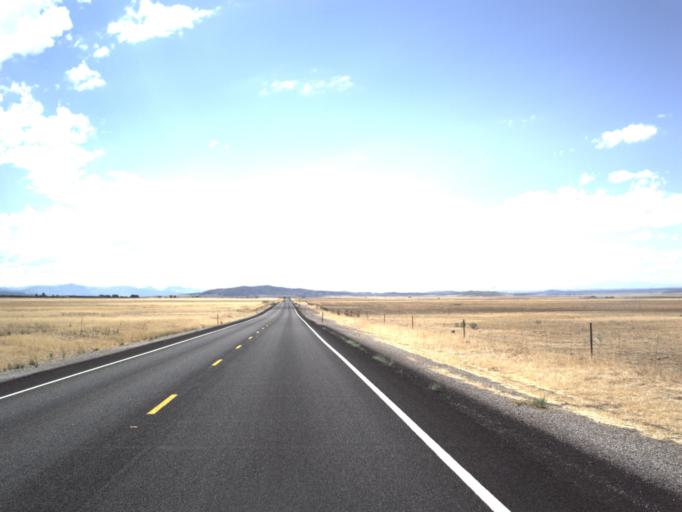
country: US
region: Utah
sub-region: Millard County
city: Fillmore
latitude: 39.1356
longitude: -112.2461
